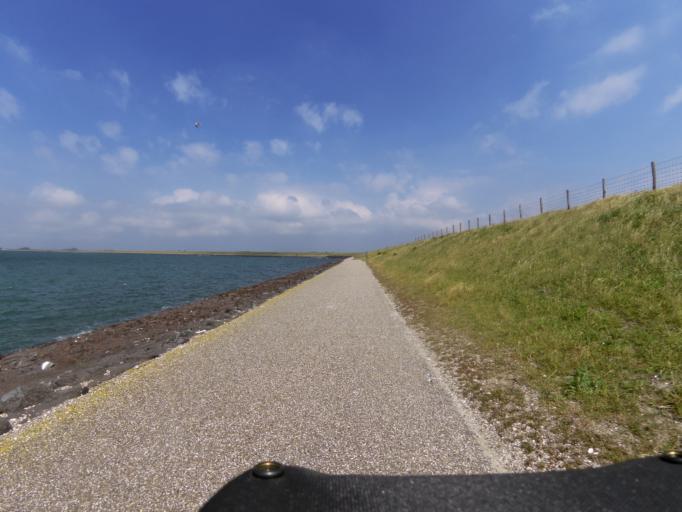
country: NL
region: Zeeland
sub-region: Schouwen-Duiveland
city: Scharendijke
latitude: 51.6640
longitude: 3.8761
